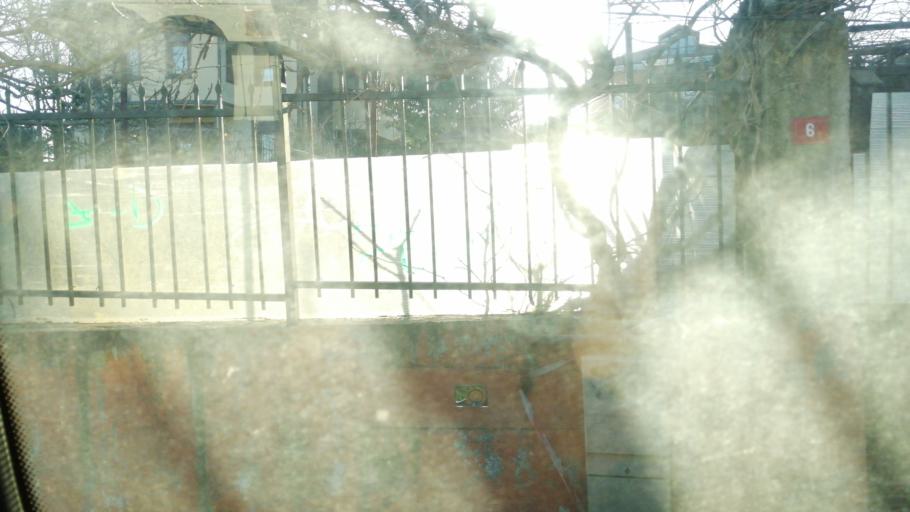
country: TR
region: Istanbul
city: UEskuedar
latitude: 41.0570
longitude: 29.0663
